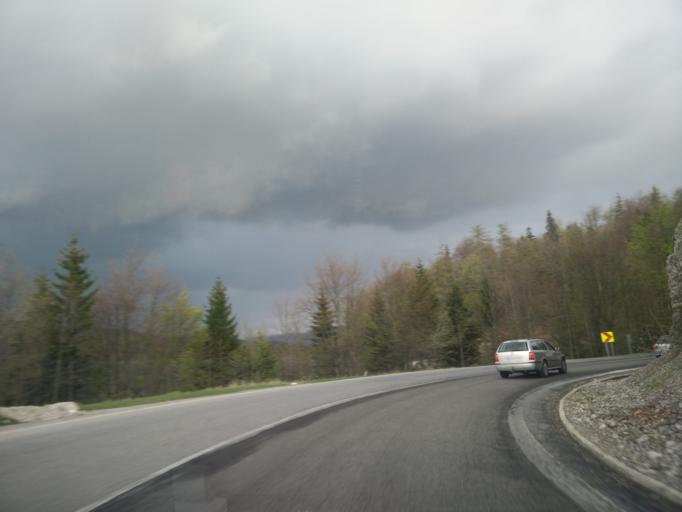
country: SK
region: Banskobystricky
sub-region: Okres Ziar nad Hronom
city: Kremnica
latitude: 48.8358
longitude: 19.0097
